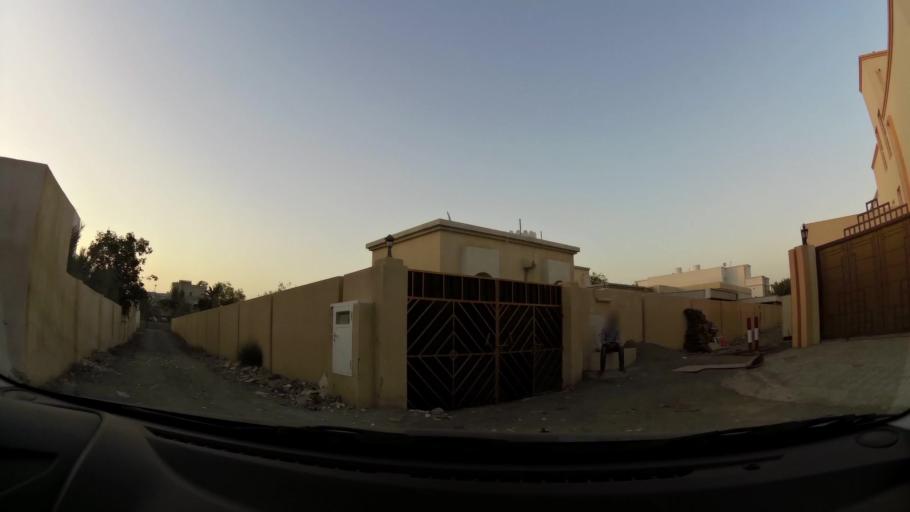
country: OM
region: Muhafazat Masqat
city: As Sib al Jadidah
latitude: 23.6459
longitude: 58.2050
